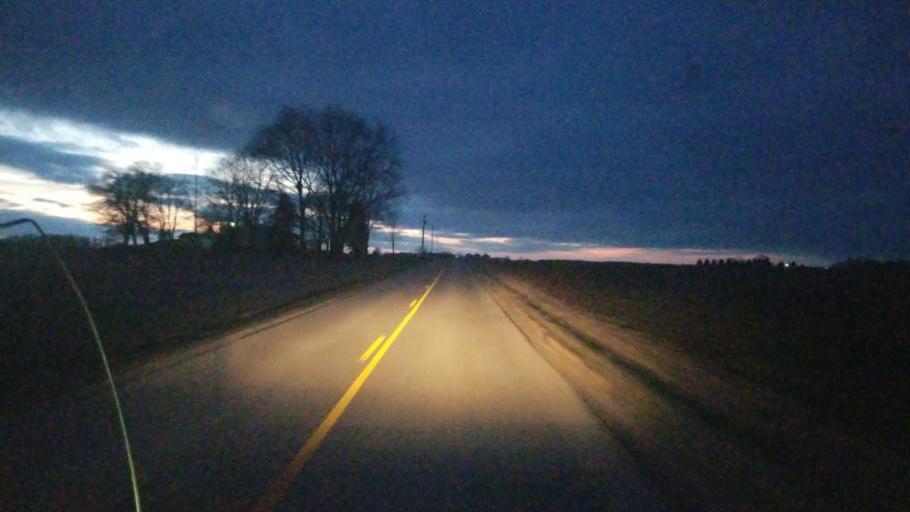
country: US
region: Ohio
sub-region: Marion County
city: Prospect
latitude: 40.4657
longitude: -83.2163
